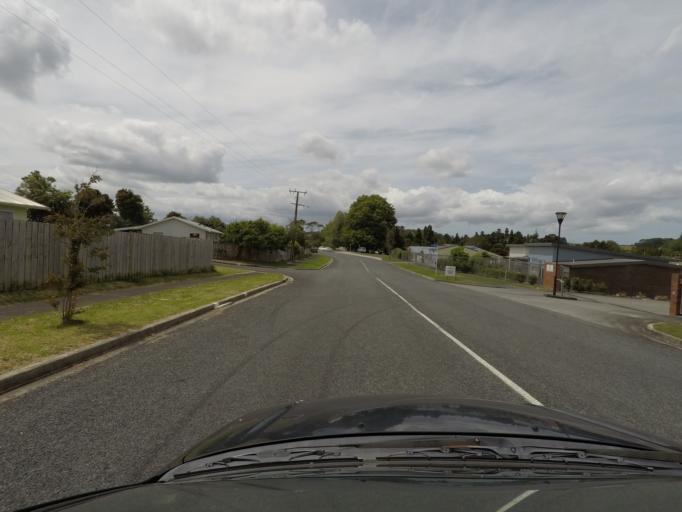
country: NZ
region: Northland
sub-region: Whangarei
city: Whangarei
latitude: -35.6857
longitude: 174.3343
